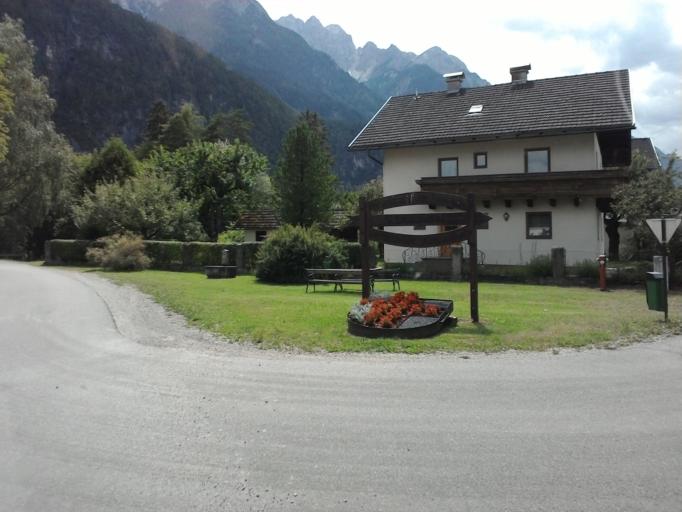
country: AT
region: Tyrol
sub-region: Politischer Bezirk Lienz
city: Leisach
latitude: 46.8062
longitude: 12.7511
